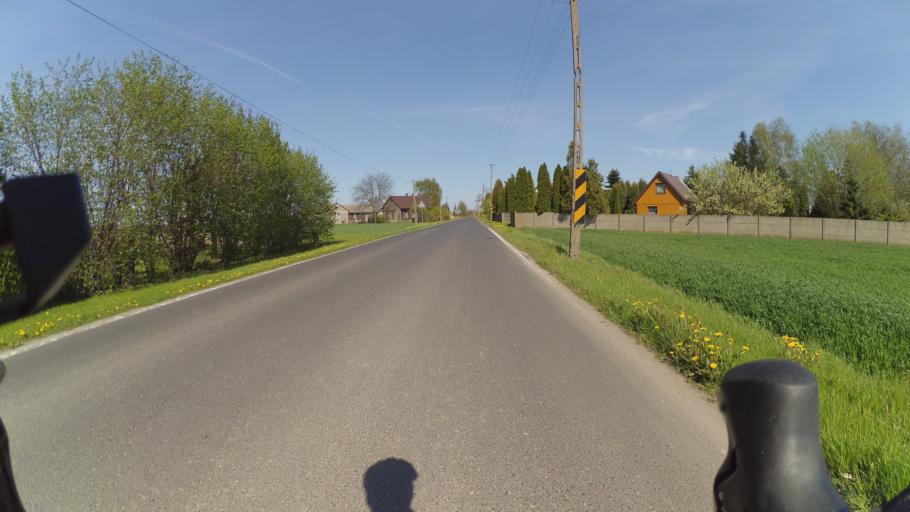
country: PL
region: Masovian Voivodeship
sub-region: Powiat warszawski zachodni
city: Leszno
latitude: 52.2463
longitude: 20.5504
